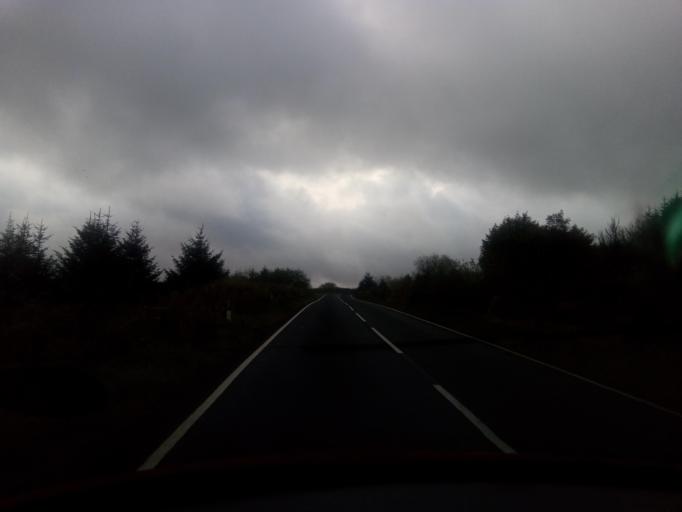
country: GB
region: Scotland
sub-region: The Scottish Borders
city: Hawick
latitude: 55.3267
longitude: -2.6467
